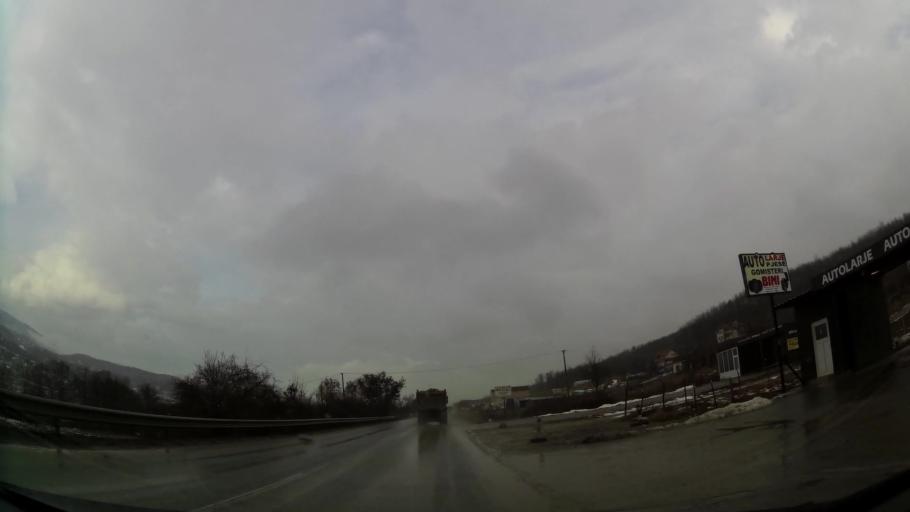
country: XK
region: Ferizaj
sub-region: Komuna e Kacanikut
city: Kacanik
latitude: 42.2418
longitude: 21.2429
